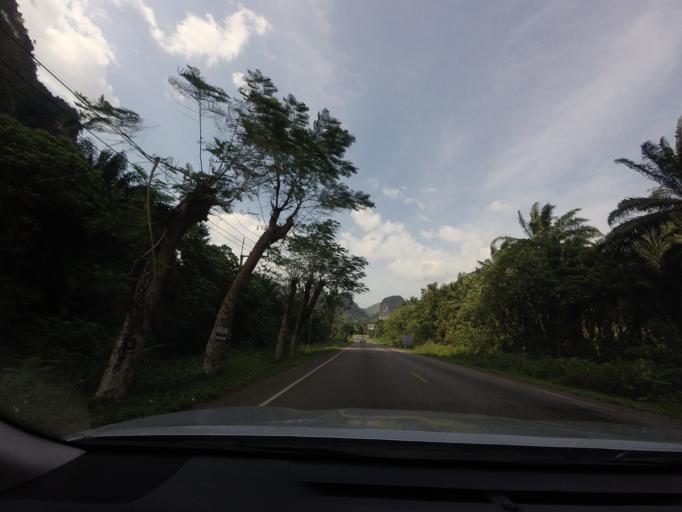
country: TH
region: Phangnga
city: Ban Ao Nang
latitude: 8.1436
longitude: 98.8119
